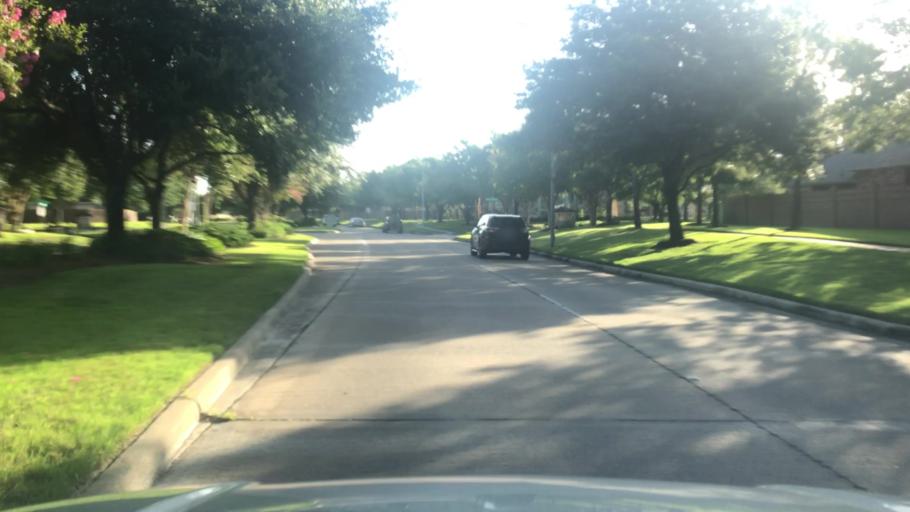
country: US
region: Texas
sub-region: Fort Bend County
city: Cinco Ranch
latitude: 29.7457
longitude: -95.7889
